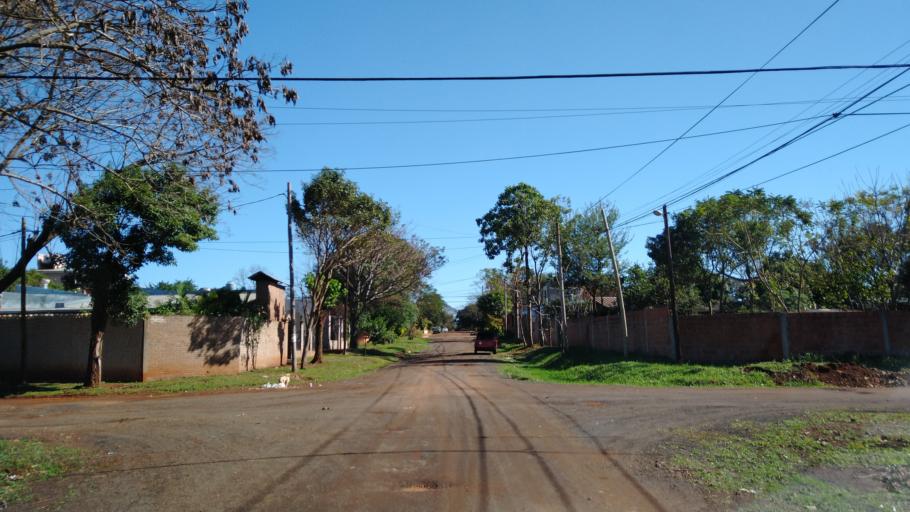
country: AR
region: Misiones
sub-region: Departamento de Capital
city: Posadas
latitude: -27.3891
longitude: -55.9260
